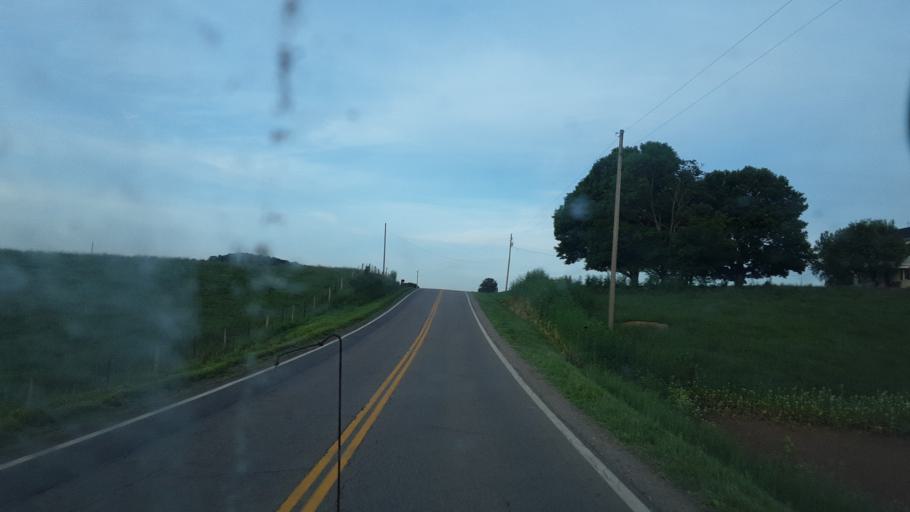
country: US
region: Ohio
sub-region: Ross County
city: Kingston
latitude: 39.4593
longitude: -82.7659
